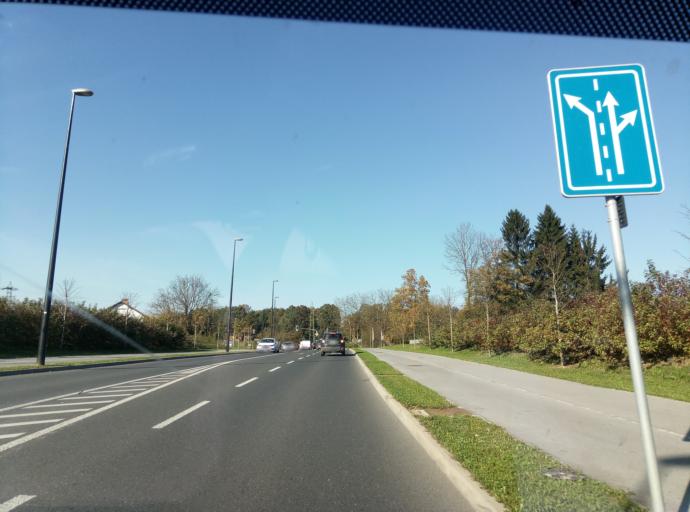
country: SI
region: Ljubljana
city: Ljubljana
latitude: 46.0390
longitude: 14.4649
